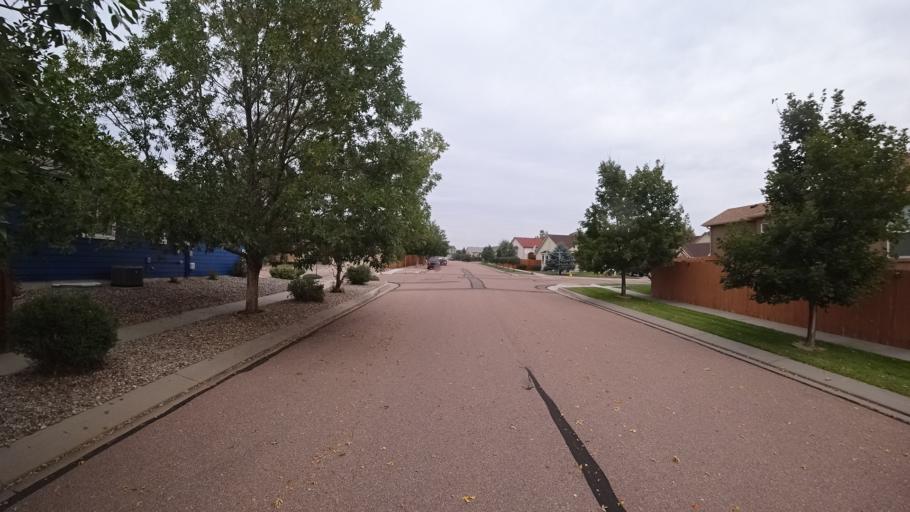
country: US
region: Colorado
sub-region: El Paso County
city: Cimarron Hills
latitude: 38.9147
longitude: -104.6897
